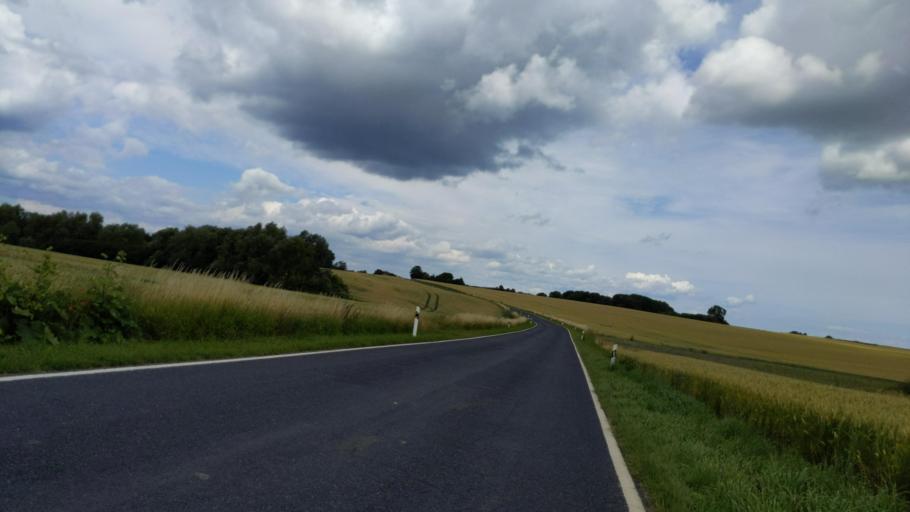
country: DE
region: Mecklenburg-Vorpommern
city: Dassow
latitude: 53.9463
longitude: 10.9732
